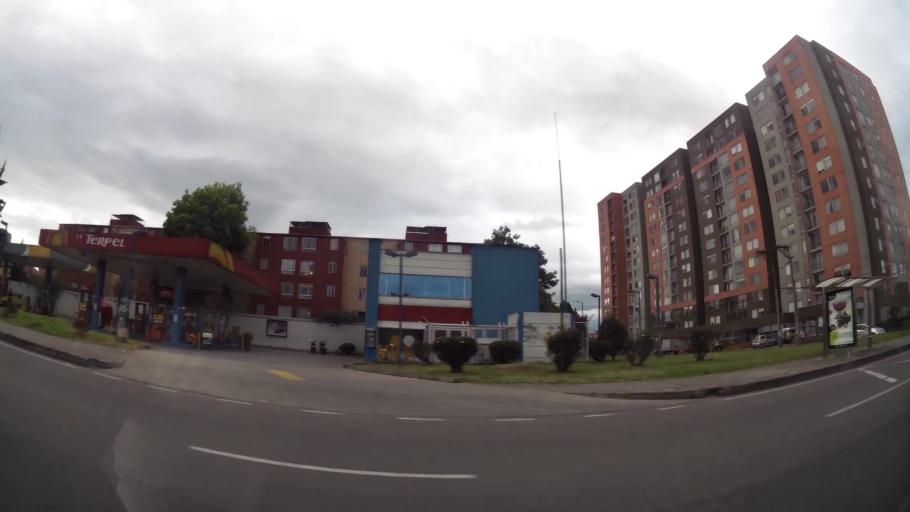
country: CO
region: Bogota D.C.
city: Barrio San Luis
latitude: 4.6980
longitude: -74.1048
